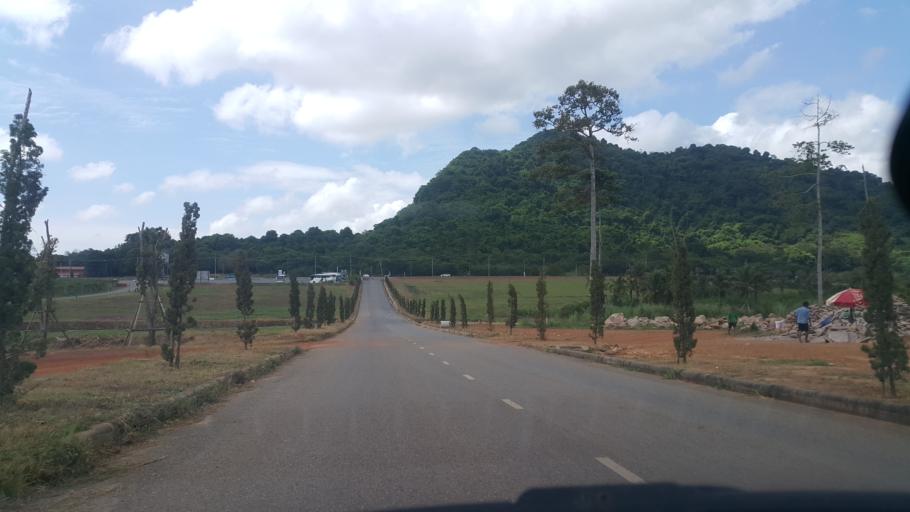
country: TH
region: Rayong
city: Ban Chang
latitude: 12.7565
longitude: 100.9661
